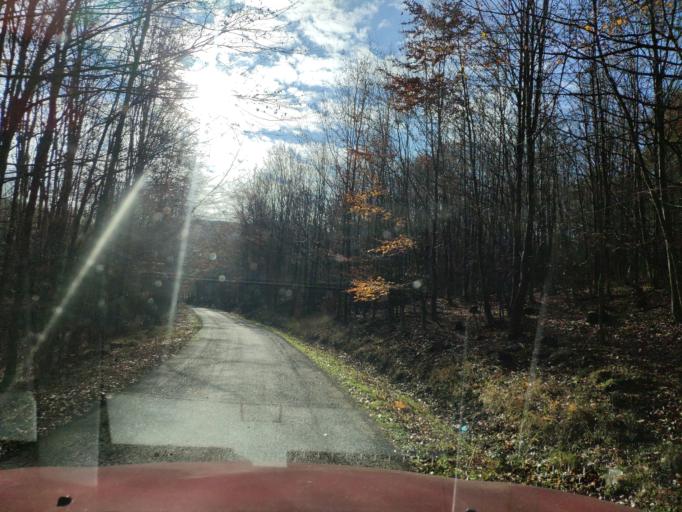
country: HU
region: Borsod-Abauj-Zemplen
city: Gonc
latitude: 48.6029
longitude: 21.4514
